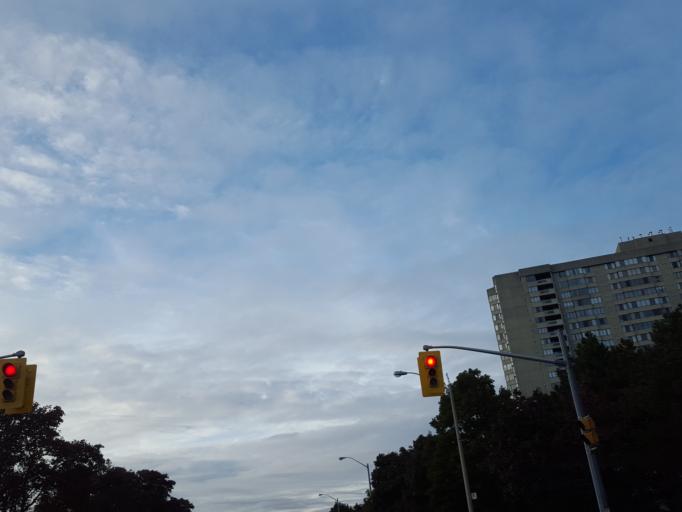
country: CA
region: Ontario
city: Scarborough
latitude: 43.7991
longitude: -79.3168
